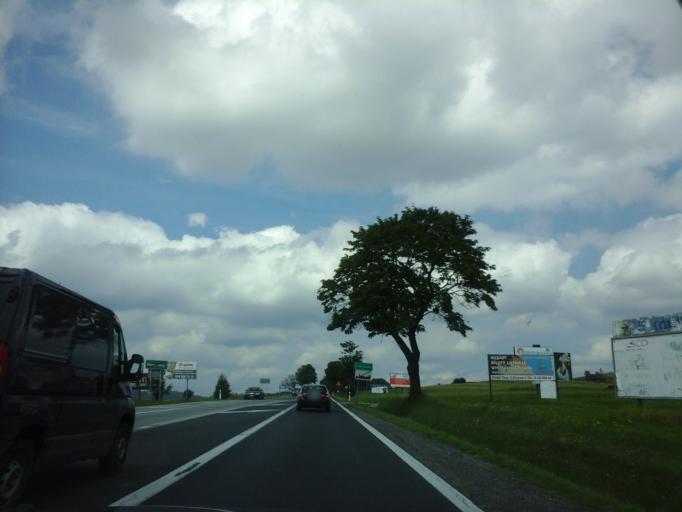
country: PL
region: Lesser Poland Voivodeship
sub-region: Powiat nowotarski
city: Lasek
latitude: 49.5043
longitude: 19.9953
